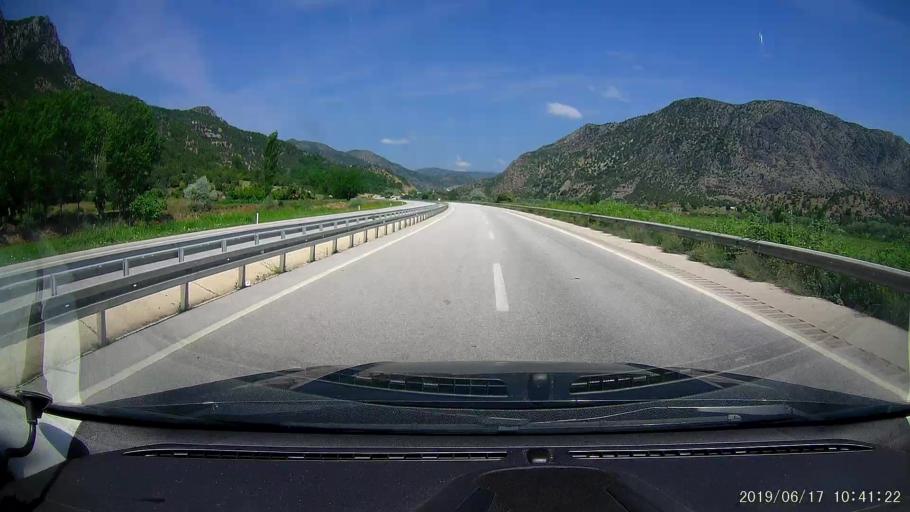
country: TR
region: Corum
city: Kargi
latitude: 41.0388
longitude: 34.5785
